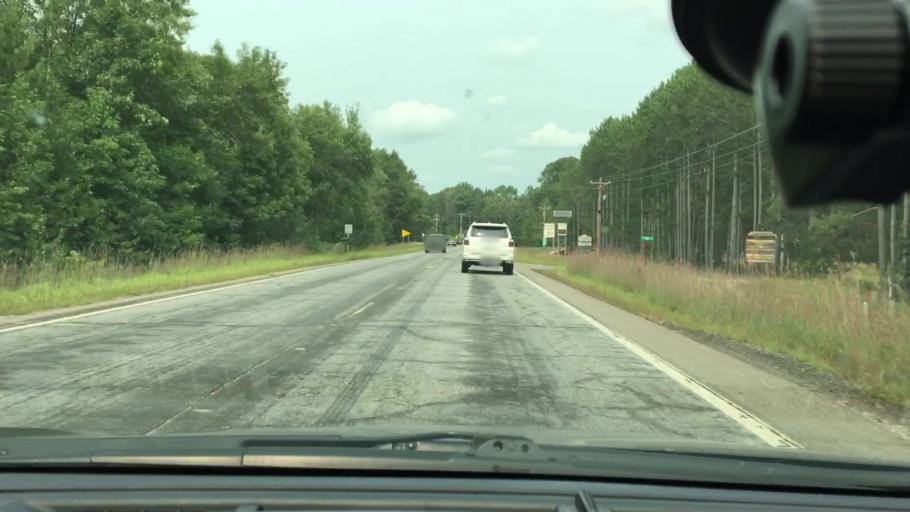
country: US
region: Minnesota
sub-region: Crow Wing County
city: Cross Lake
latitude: 46.8146
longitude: -93.9447
